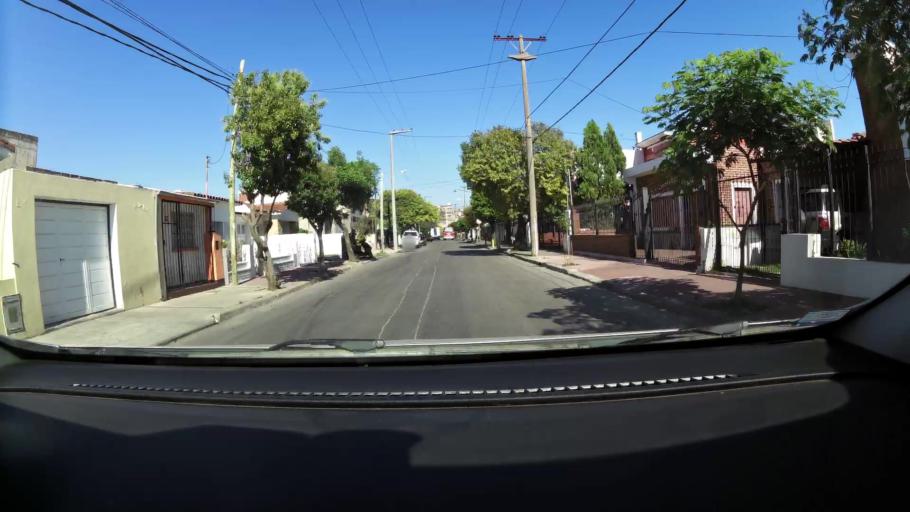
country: AR
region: Cordoba
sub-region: Departamento de Capital
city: Cordoba
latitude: -31.4289
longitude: -64.1658
